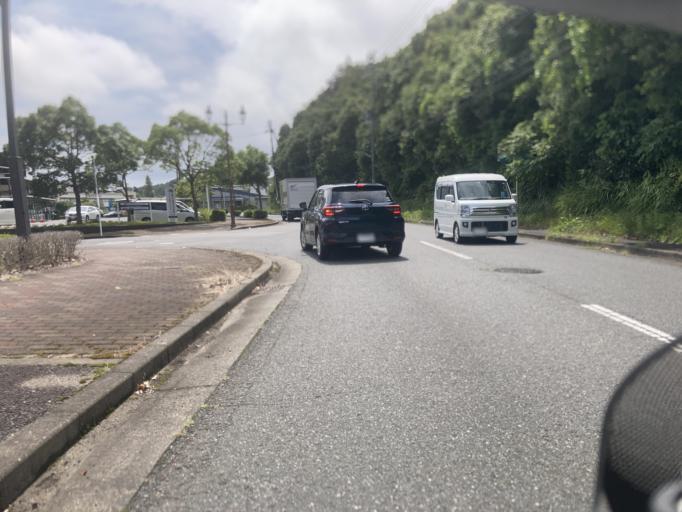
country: JP
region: Fukushima
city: Iwaki
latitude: 37.0160
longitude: 140.9194
